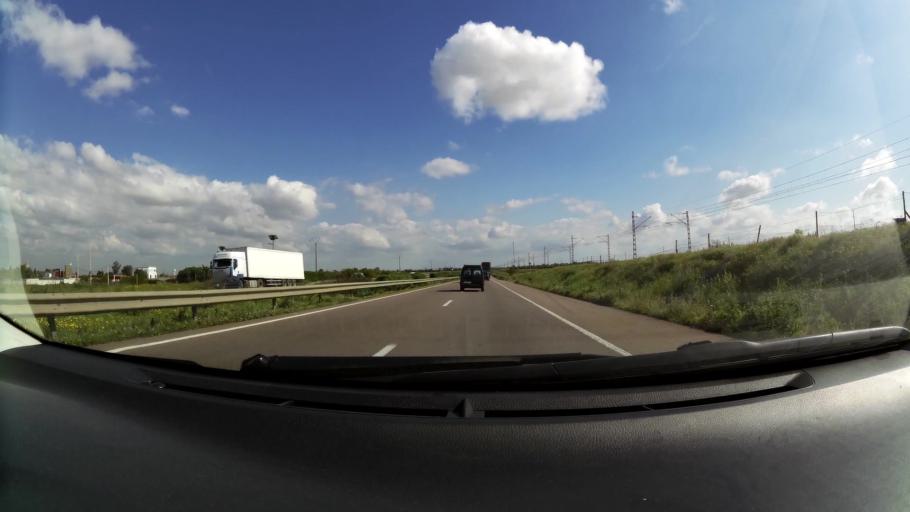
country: MA
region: Chaouia-Ouardigha
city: Nouaseur
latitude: 33.3488
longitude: -7.6152
